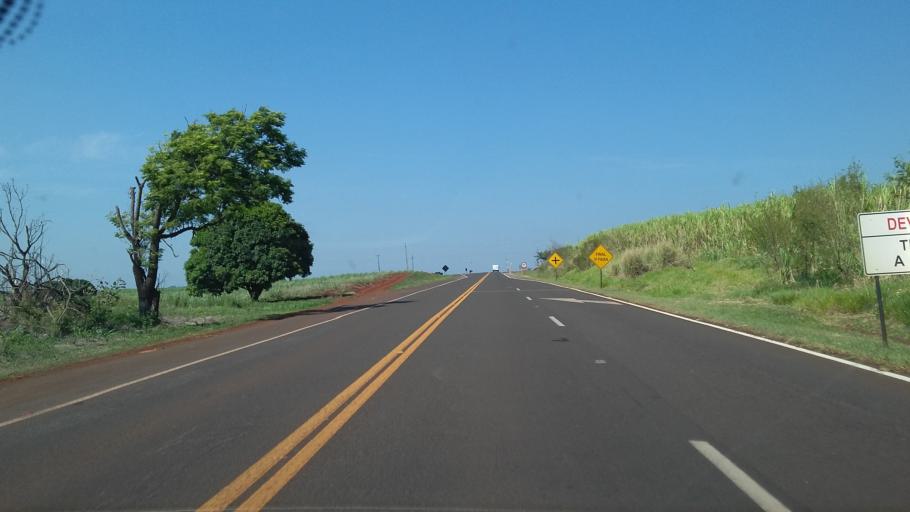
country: BR
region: Parana
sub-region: Bandeirantes
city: Bandeirantes
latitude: -23.1233
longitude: -50.3554
